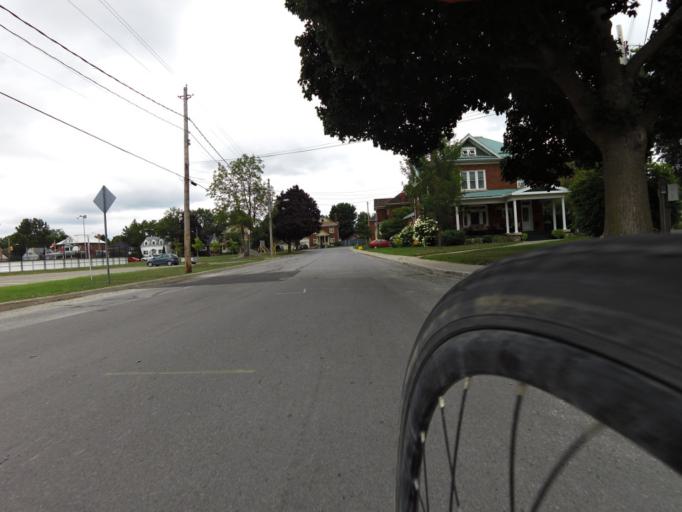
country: CA
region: Ontario
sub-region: Lanark County
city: Smiths Falls
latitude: 44.9053
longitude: -76.0252
